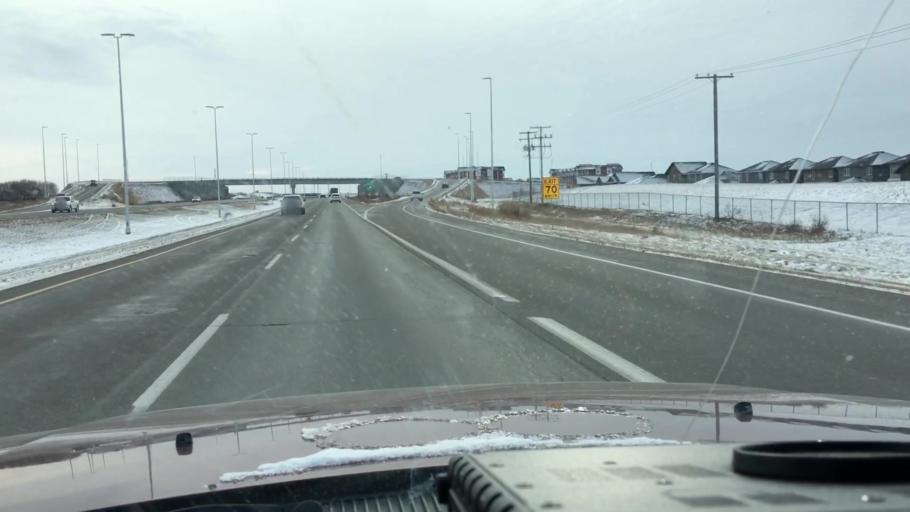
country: CA
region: Saskatchewan
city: Saskatoon
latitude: 52.0812
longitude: -106.6050
